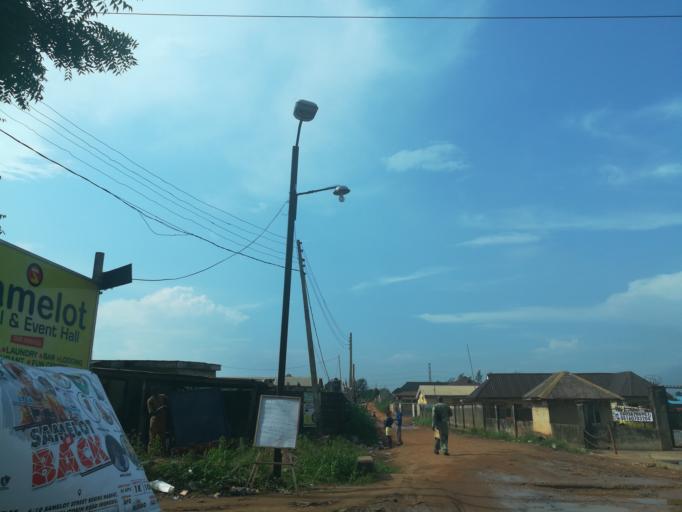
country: NG
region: Lagos
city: Ikorodu
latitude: 6.6308
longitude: 3.5231
